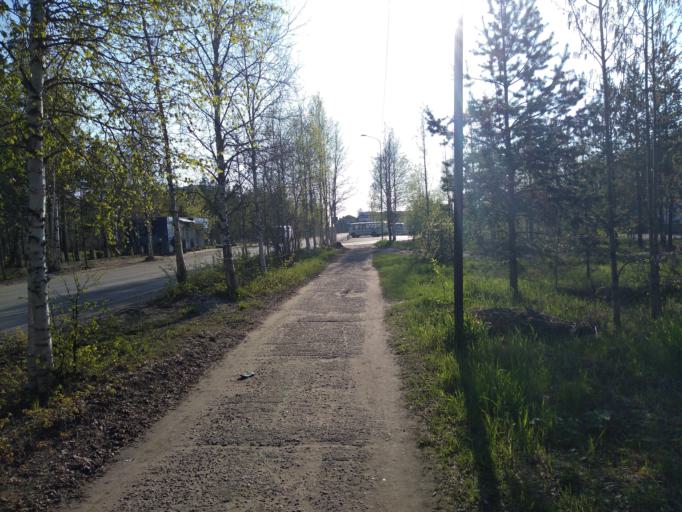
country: RU
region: Komi Republic
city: Puteyets
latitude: 65.1094
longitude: 57.1463
